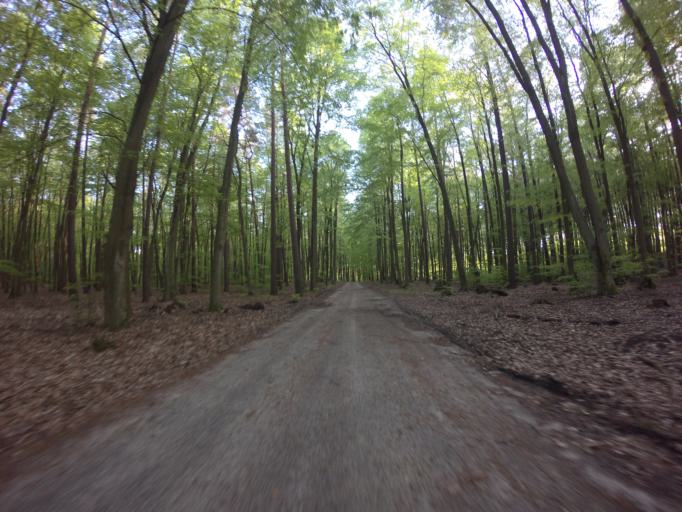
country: PL
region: West Pomeranian Voivodeship
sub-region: Powiat choszczenski
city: Drawno
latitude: 53.2014
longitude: 15.6712
